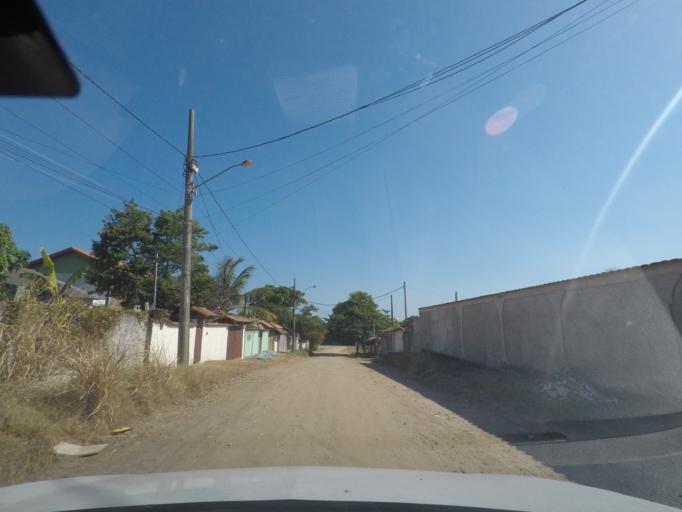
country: BR
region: Rio de Janeiro
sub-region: Marica
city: Marica
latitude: -22.9705
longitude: -42.9244
